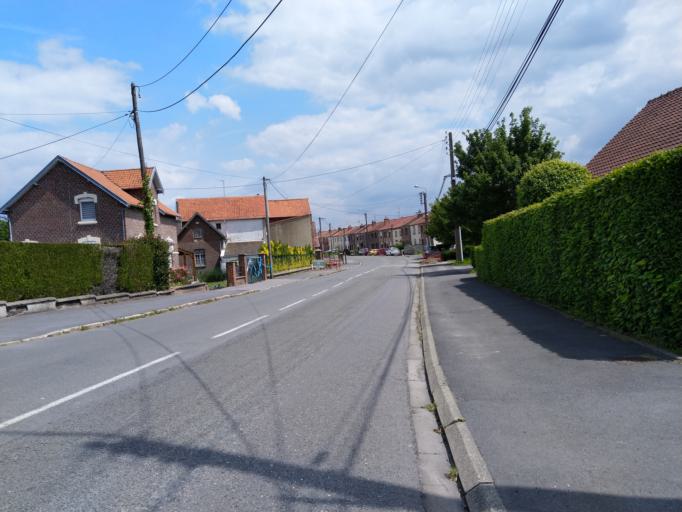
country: FR
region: Nord-Pas-de-Calais
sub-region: Departement du Nord
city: Le Quesnoy
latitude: 50.2432
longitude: 3.6504
